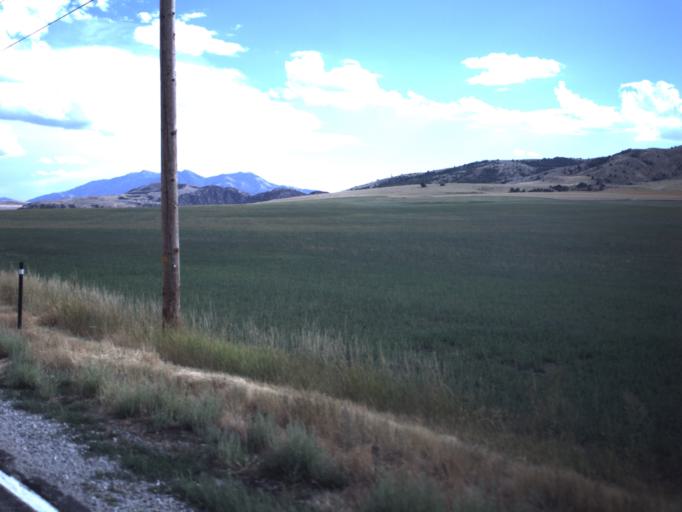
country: US
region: Utah
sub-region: Cache County
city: Benson
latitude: 41.8928
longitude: -112.0413
